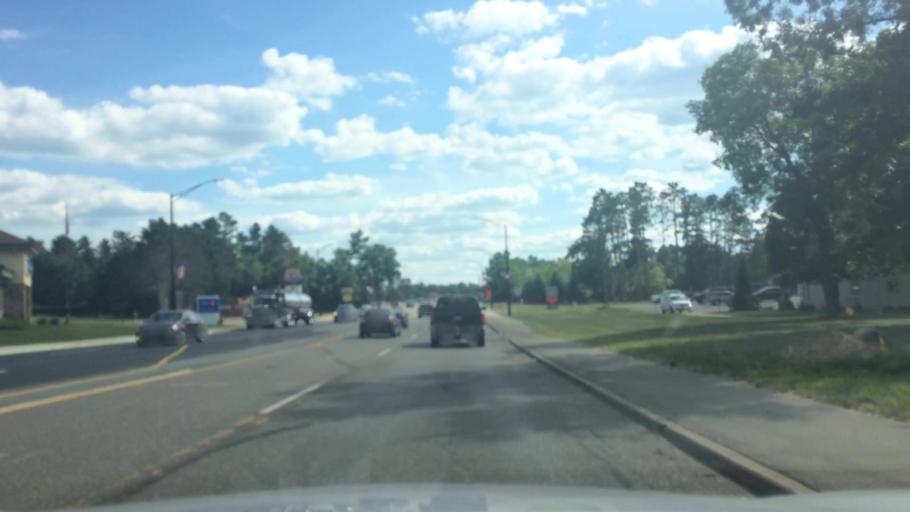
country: US
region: Wisconsin
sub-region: Vilas County
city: Lac du Flambeau
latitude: 45.8945
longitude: -89.6989
